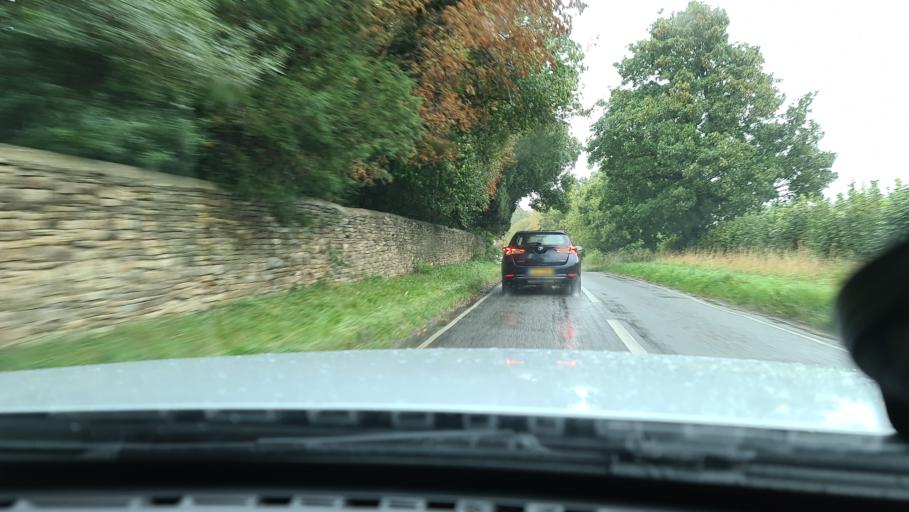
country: GB
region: England
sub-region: Oxfordshire
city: Woodstock
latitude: 51.8789
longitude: -1.3615
